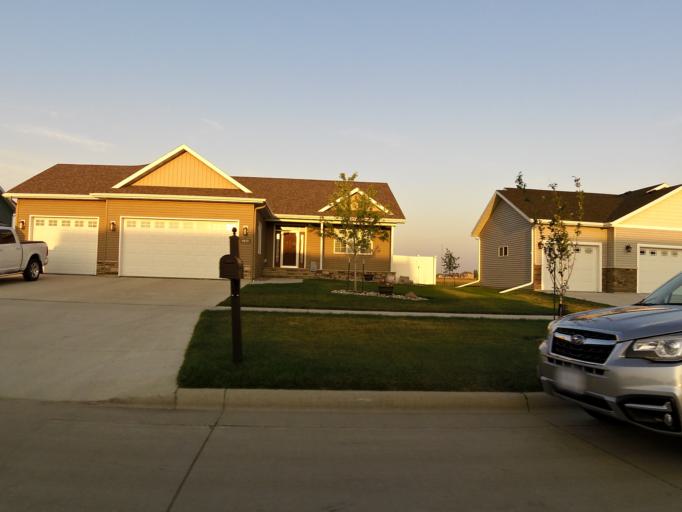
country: US
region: North Dakota
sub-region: Grand Forks County
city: Grand Forks
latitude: 47.8802
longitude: -97.0716
